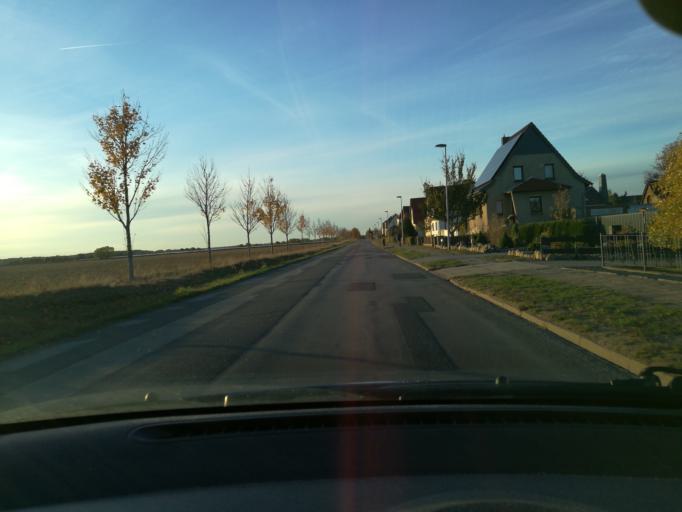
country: DE
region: Brandenburg
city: Perleberg
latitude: 53.0713
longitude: 11.8423
